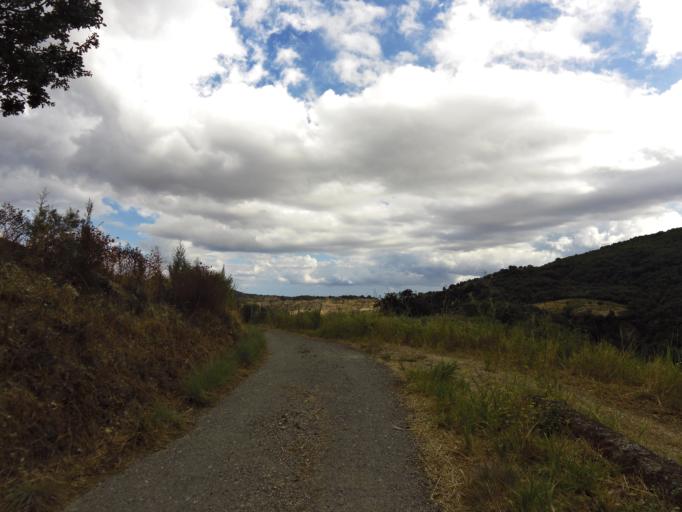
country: IT
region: Calabria
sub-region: Provincia di Reggio Calabria
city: Stignano
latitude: 38.4436
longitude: 16.4530
